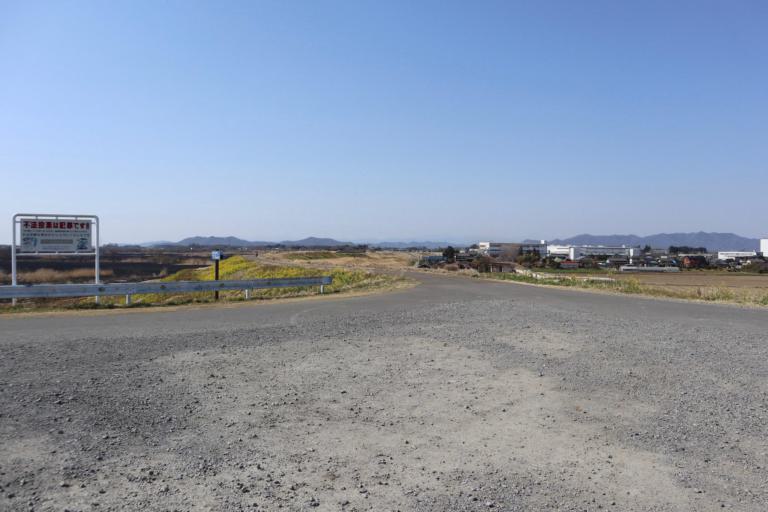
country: JP
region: Tochigi
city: Fujioka
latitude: 36.2702
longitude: 139.7017
